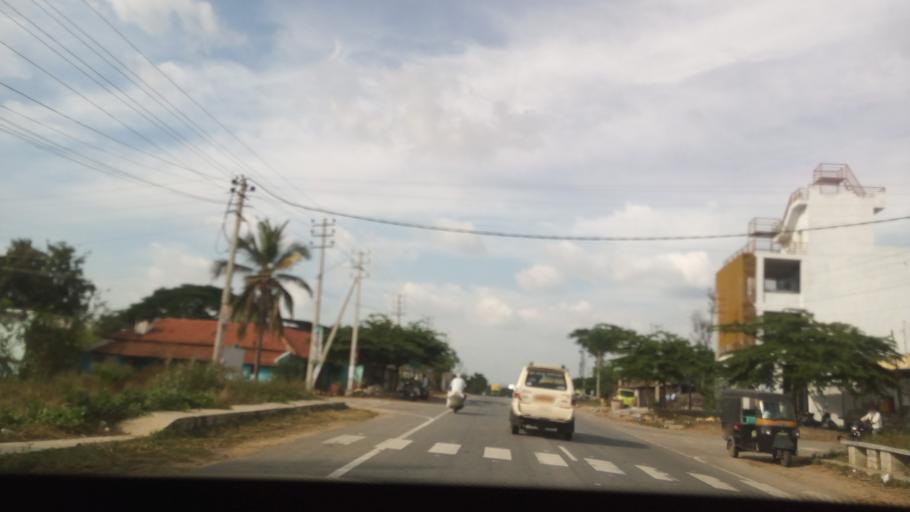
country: IN
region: Karnataka
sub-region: Mandya
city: Maddur
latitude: 12.6817
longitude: 77.0589
